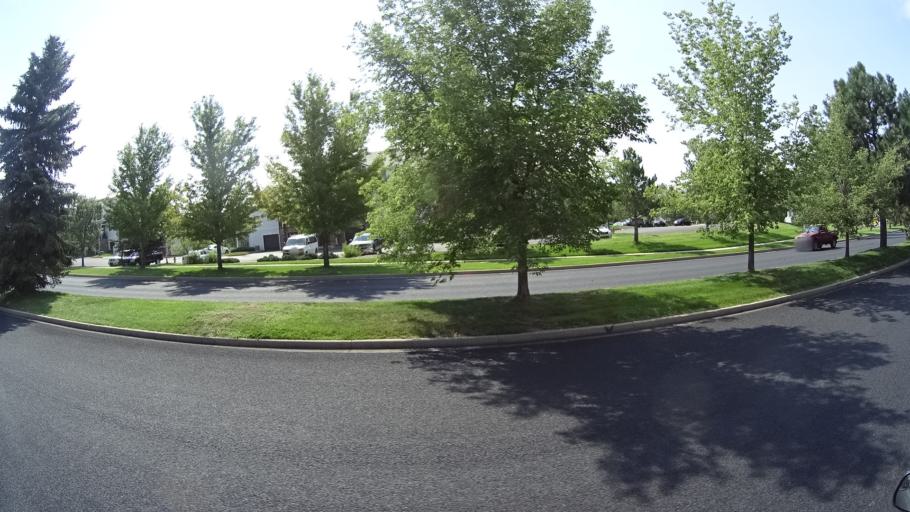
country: US
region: Colorado
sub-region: El Paso County
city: Cimarron Hills
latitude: 38.9307
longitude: -104.7474
